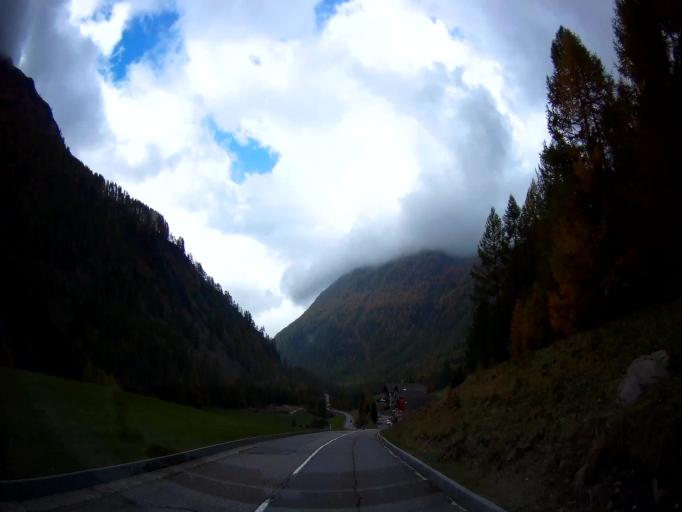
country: IT
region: Trentino-Alto Adige
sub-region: Bolzano
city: Senales
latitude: 46.7345
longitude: 10.8011
